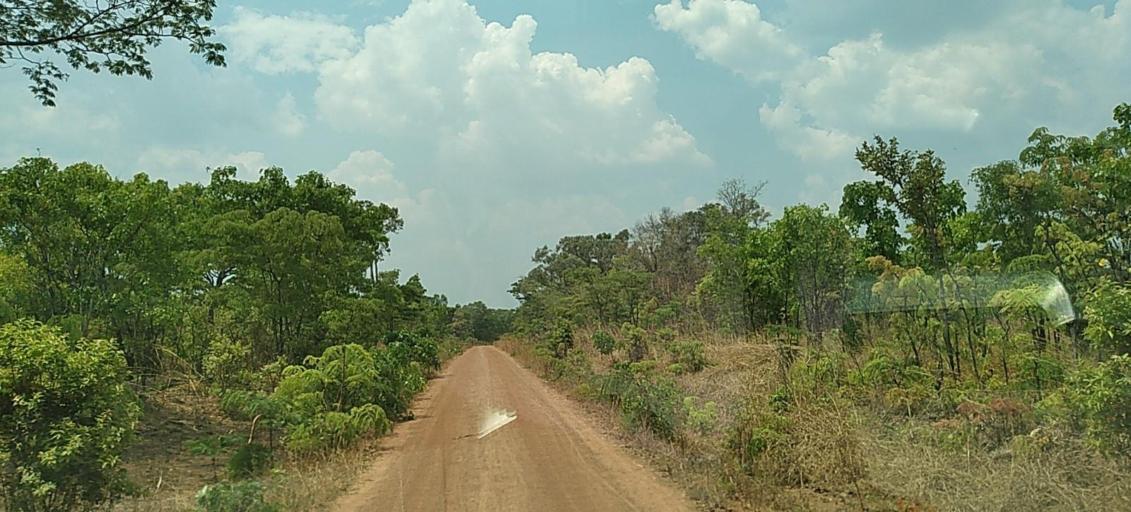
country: ZM
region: Copperbelt
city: Chingola
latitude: -12.6867
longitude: 27.7201
